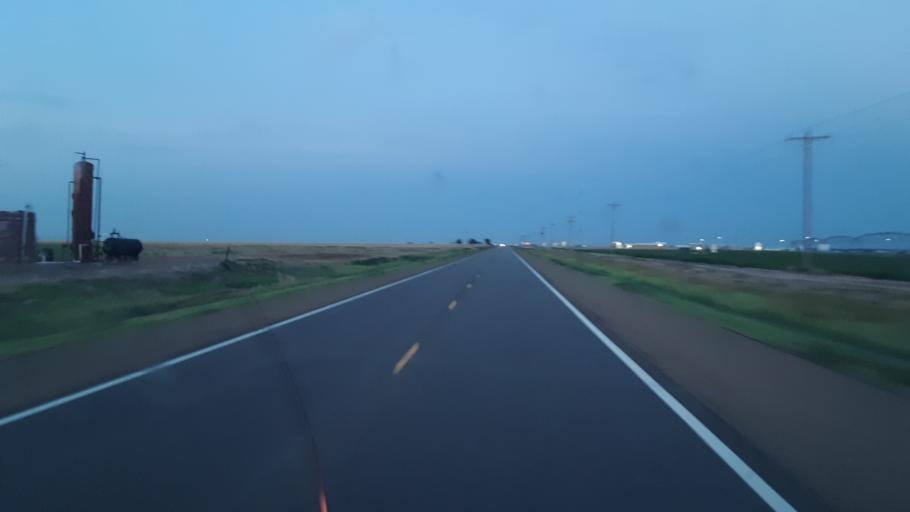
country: US
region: Kansas
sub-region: Finney County
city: Holcomb
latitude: 38.0034
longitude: -101.0437
